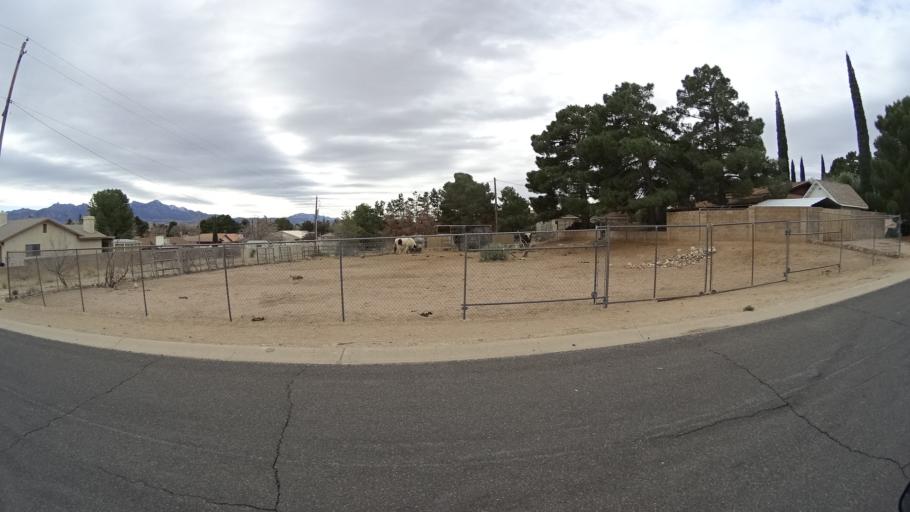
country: US
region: Arizona
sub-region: Mohave County
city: New Kingman-Butler
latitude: 35.2363
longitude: -114.0452
